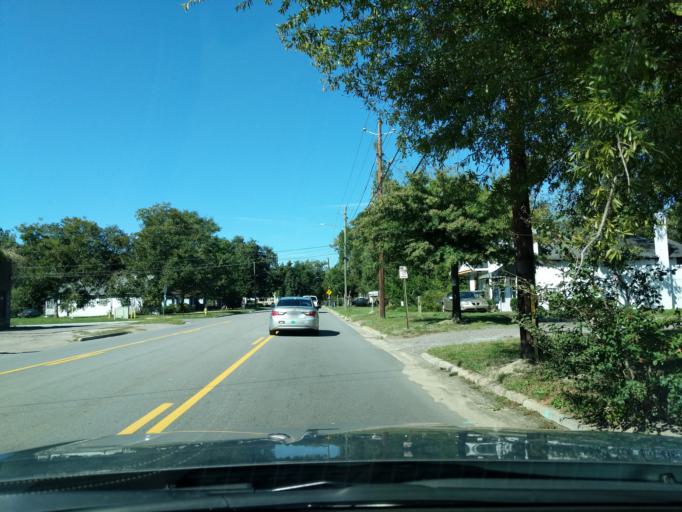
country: US
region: Georgia
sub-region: Richmond County
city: Augusta
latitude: 33.4424
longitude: -82.0027
